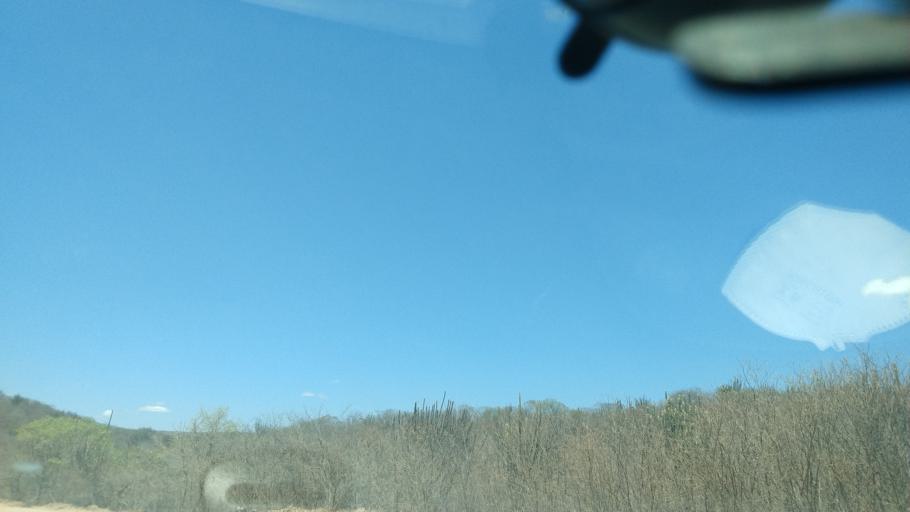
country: BR
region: Rio Grande do Norte
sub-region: Cerro Cora
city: Cerro Cora
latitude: -6.0102
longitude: -36.2789
